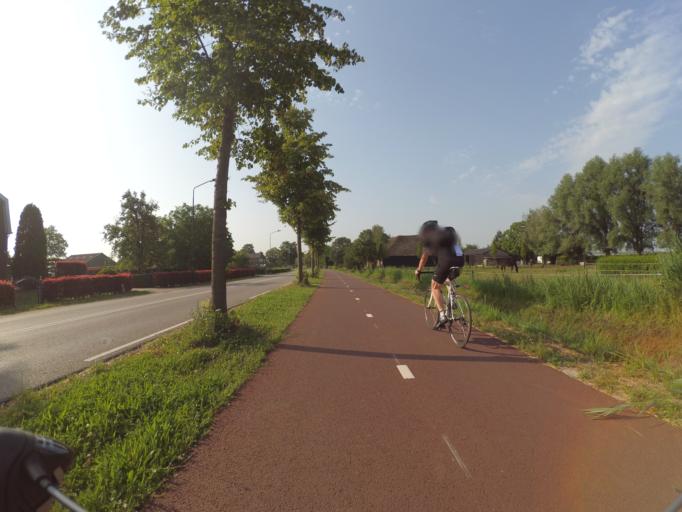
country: NL
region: North Brabant
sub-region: Gemeente Dongen
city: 's Gravenmoer
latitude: 51.6486
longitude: 4.9423
